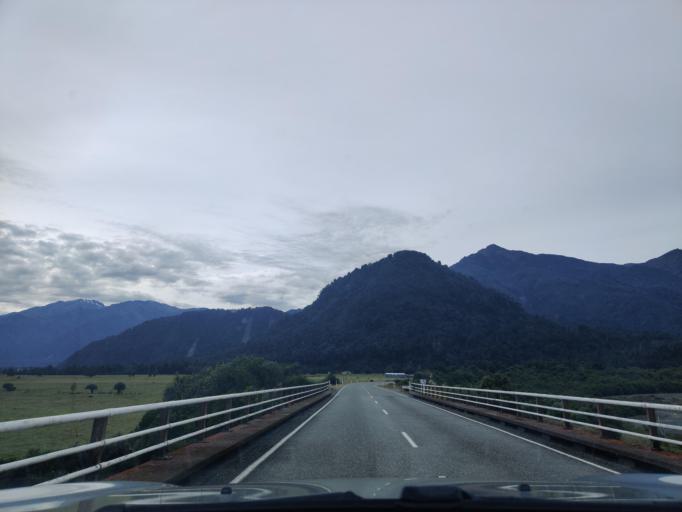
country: NZ
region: West Coast
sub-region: Westland District
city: Hokitika
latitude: -43.2825
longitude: 170.3070
